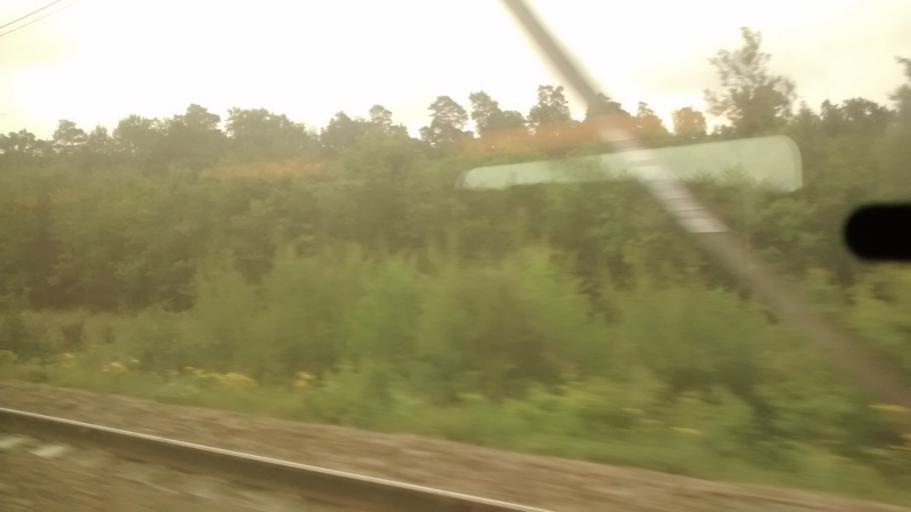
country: FR
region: Bourgogne
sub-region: Departement de l'Yonne
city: Vergigny
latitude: 47.9633
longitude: 3.7169
